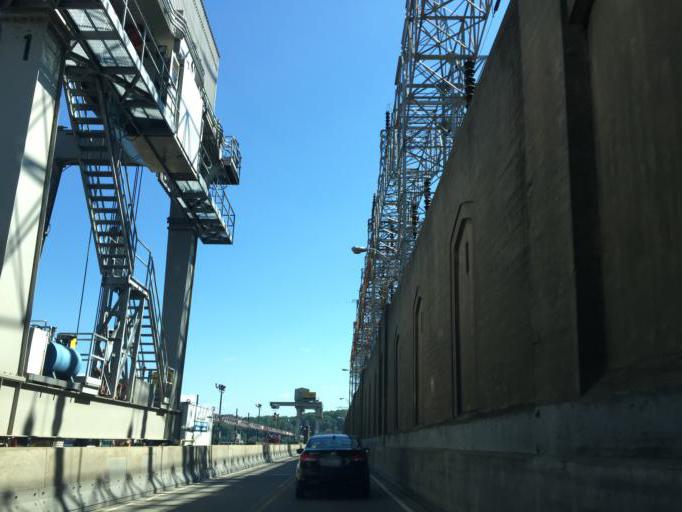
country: US
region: Maryland
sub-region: Cecil County
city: Rising Sun
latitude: 39.6568
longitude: -76.1756
